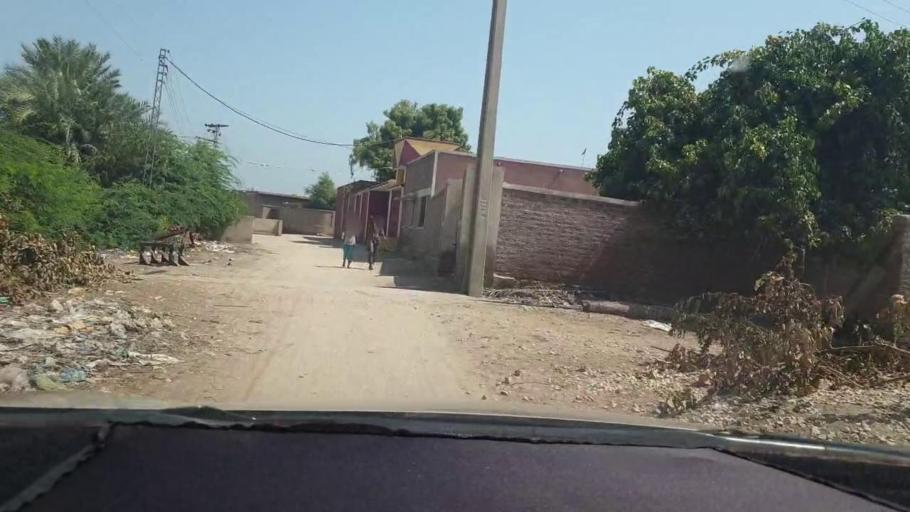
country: PK
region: Sindh
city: Kambar
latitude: 27.5896
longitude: 68.0626
